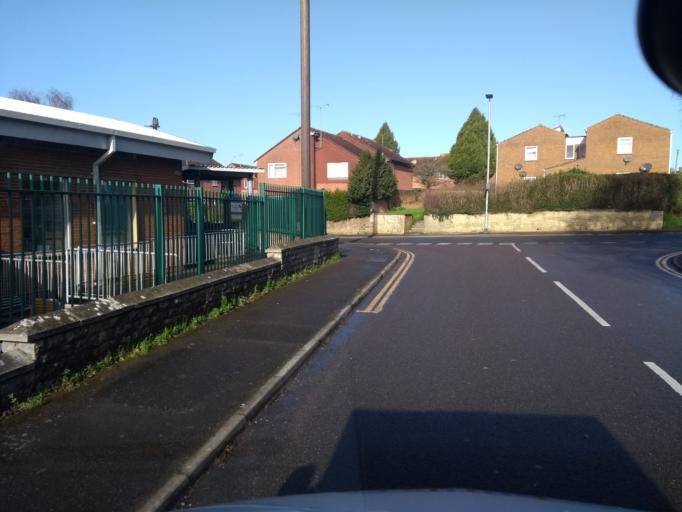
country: GB
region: England
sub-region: Somerset
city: Yeovil
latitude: 50.9476
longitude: -2.6111
